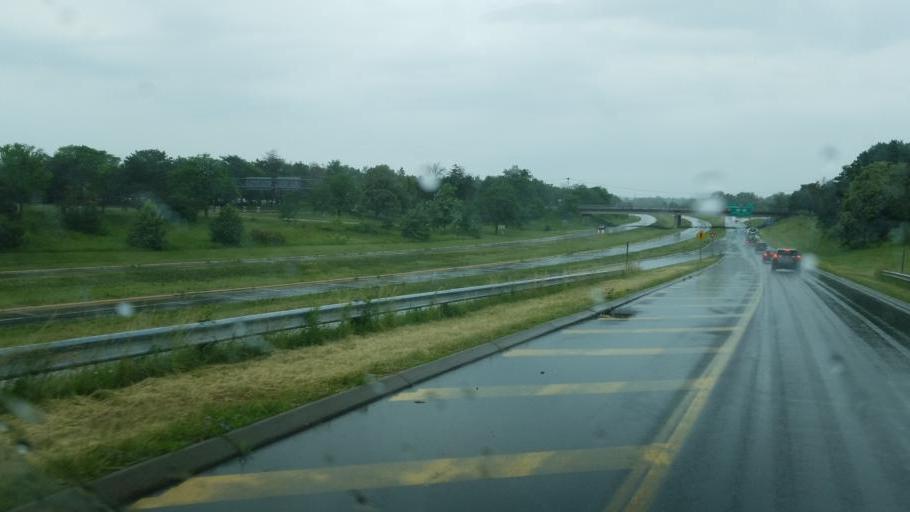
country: US
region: New York
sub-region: Niagara County
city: Lewiston
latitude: 43.1704
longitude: -79.0294
